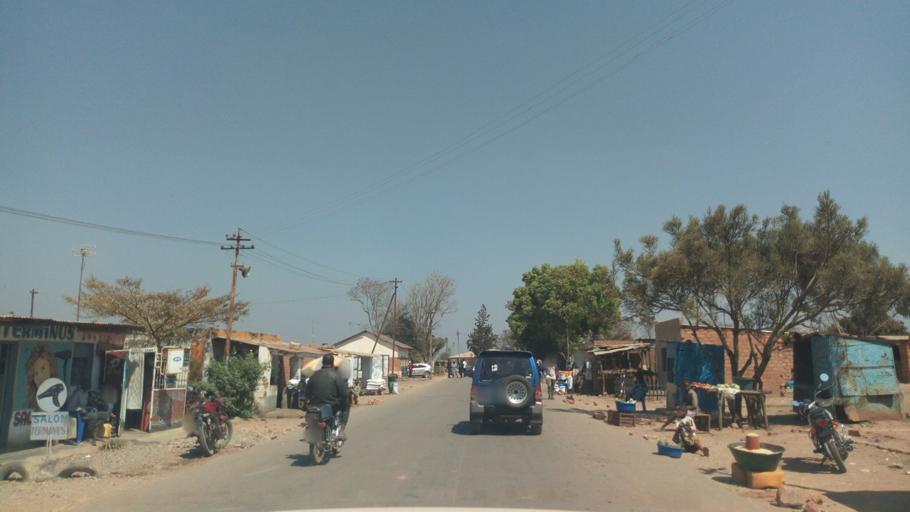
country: CD
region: Katanga
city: Kipushi
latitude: -11.7613
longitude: 27.2311
